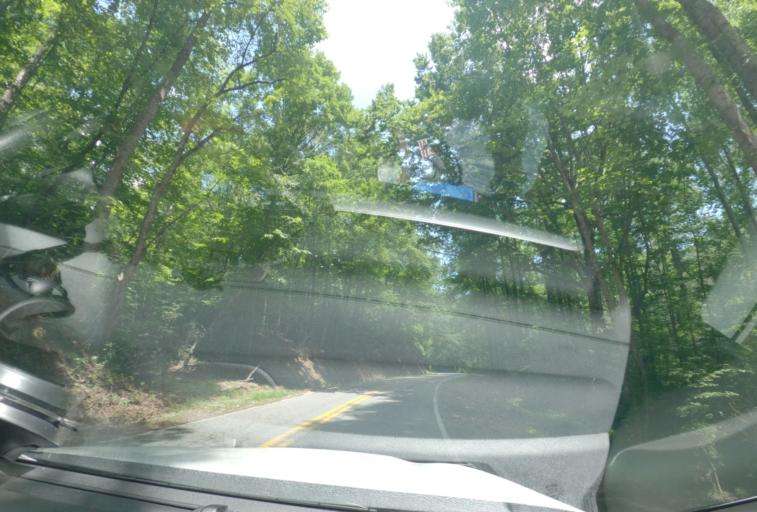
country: US
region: South Carolina
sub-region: Pickens County
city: Pickens
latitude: 34.9997
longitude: -82.8210
